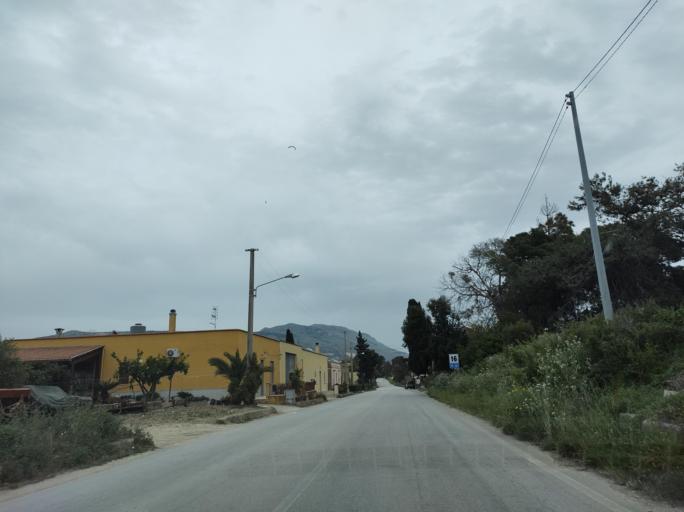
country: IT
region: Sicily
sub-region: Trapani
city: Custonaci
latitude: 38.0413
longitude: 12.6722
